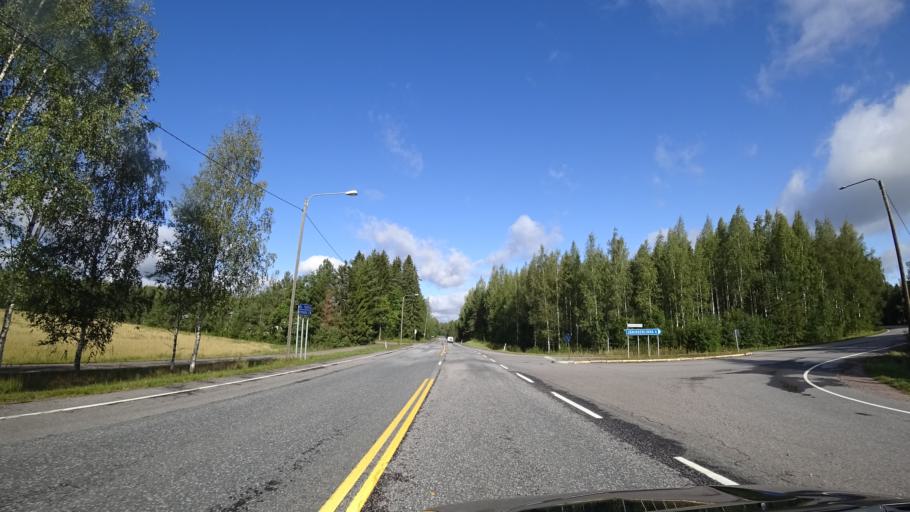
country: FI
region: Uusimaa
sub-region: Helsinki
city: Tuusula
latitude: 60.4433
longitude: 24.9733
